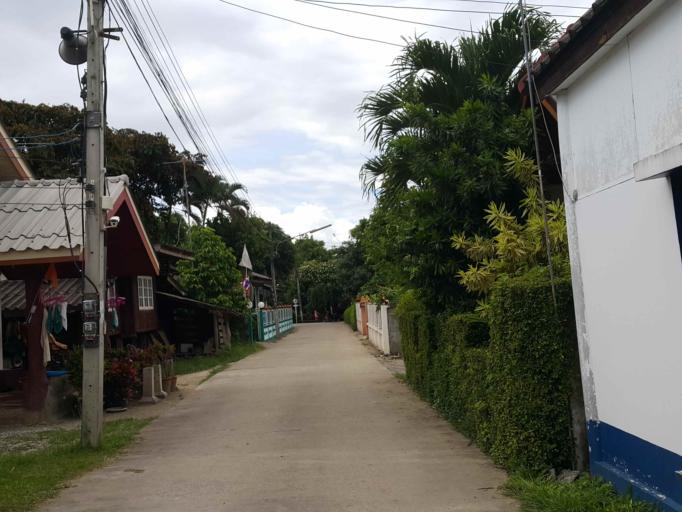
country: TH
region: Chiang Mai
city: San Sai
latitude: 18.9306
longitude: 98.9195
